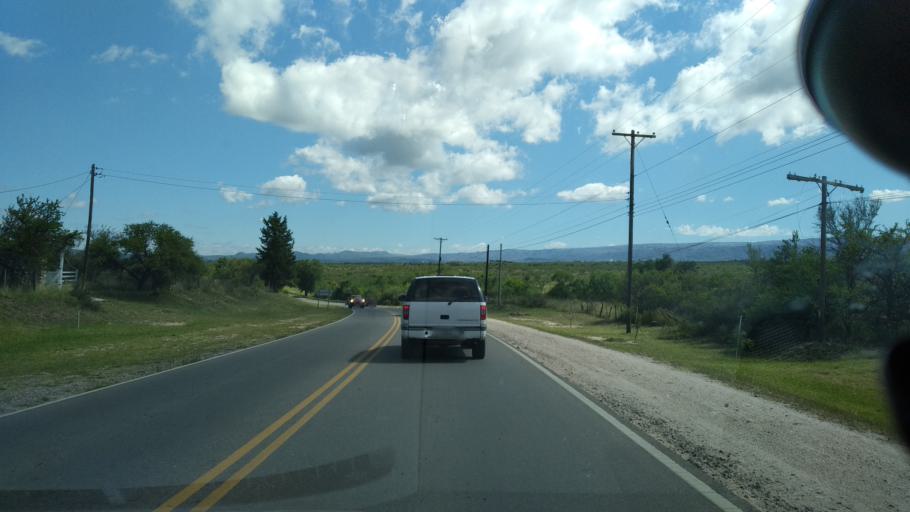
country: AR
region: Cordoba
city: Mina Clavero
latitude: -31.7887
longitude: -64.9981
